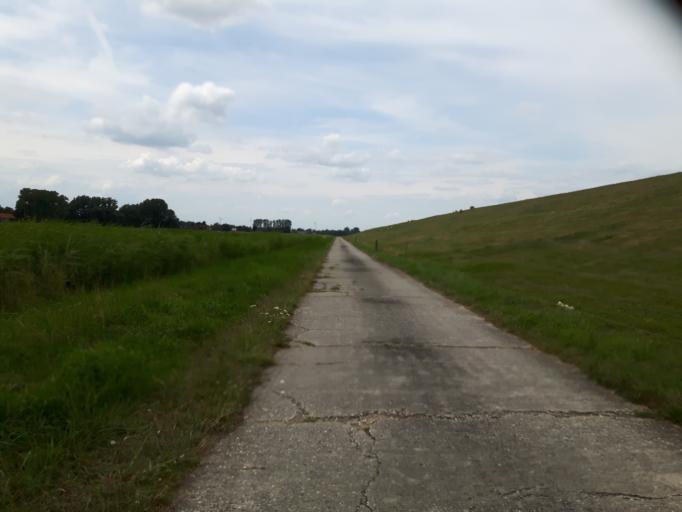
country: DE
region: Lower Saxony
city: Varel
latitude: 53.3917
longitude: 8.2499
